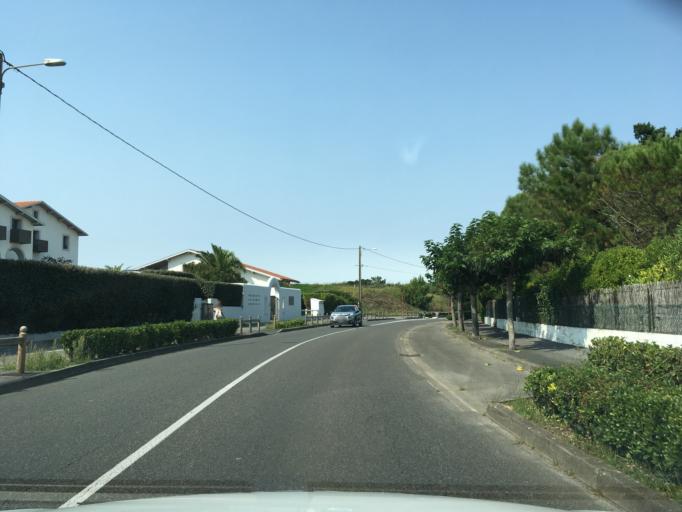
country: FR
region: Aquitaine
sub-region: Departement des Pyrenees-Atlantiques
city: Anglet
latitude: 43.5182
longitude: -1.5238
